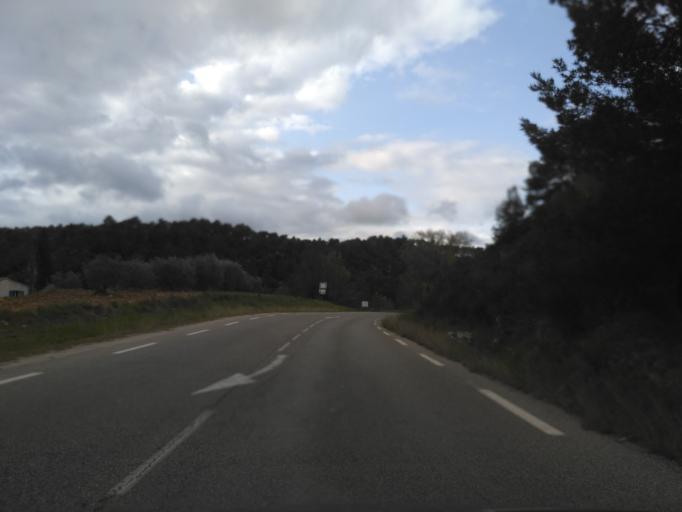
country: FR
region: Provence-Alpes-Cote d'Azur
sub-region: Departement du Var
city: Barjols
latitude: 43.5673
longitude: 6.0120
